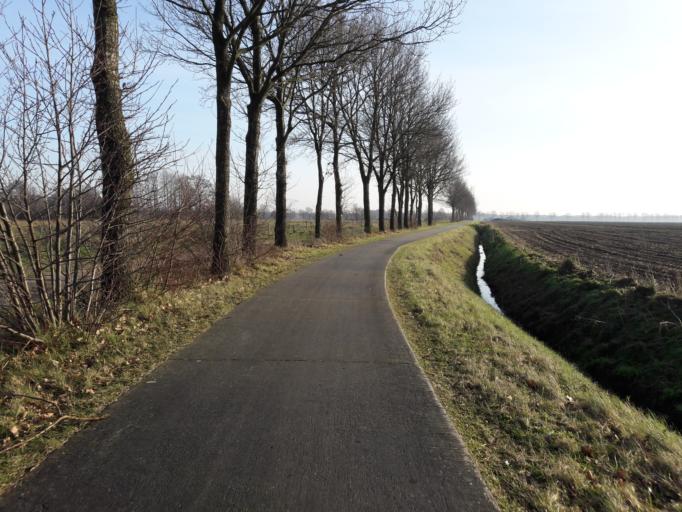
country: NL
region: Drenthe
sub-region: Gemeente Assen
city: Assen
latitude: 52.9487
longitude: 6.6354
